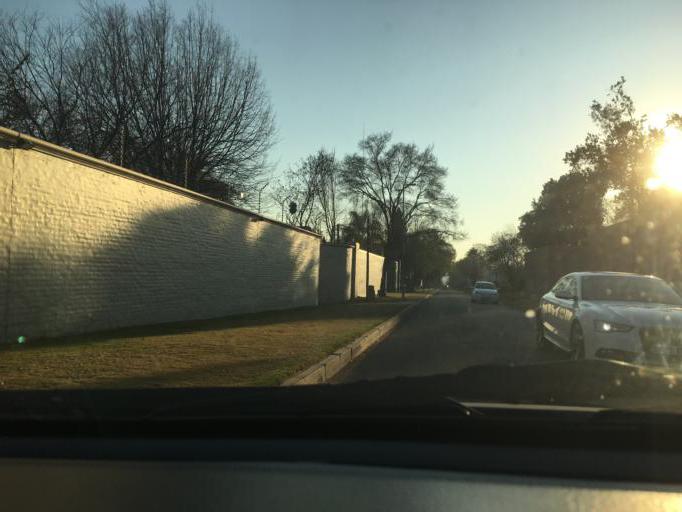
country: ZA
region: Gauteng
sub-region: City of Johannesburg Metropolitan Municipality
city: Diepsloot
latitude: -26.0685
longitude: 28.0024
